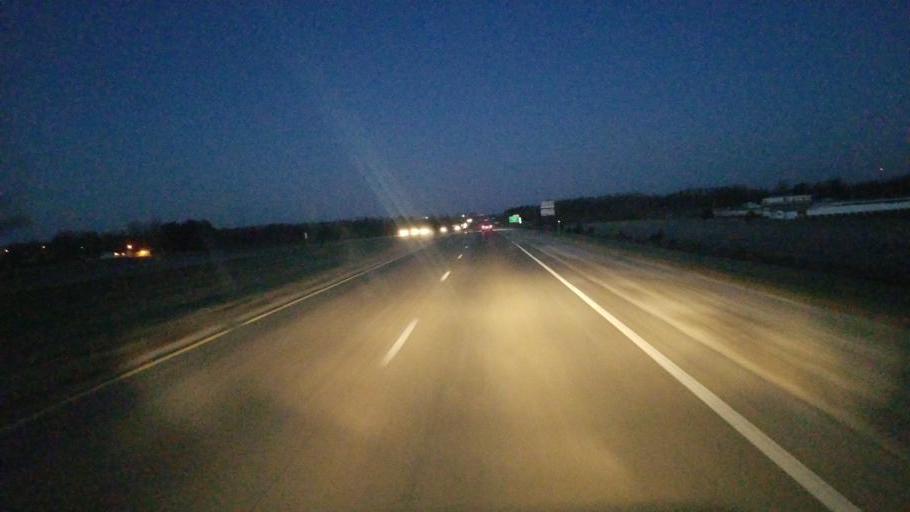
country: US
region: Iowa
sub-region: Des Moines County
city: West Burlington
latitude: 40.8325
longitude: -91.2436
